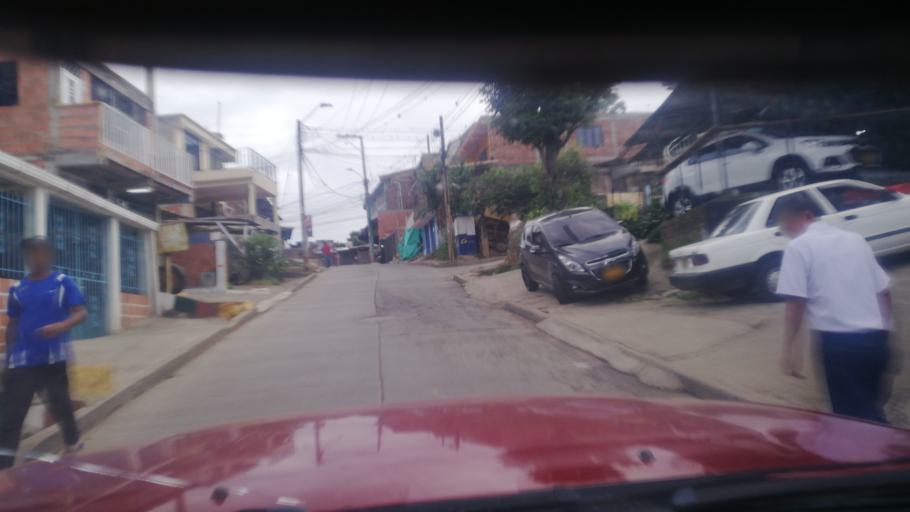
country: CO
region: Valle del Cauca
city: Cali
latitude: 3.4845
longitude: -76.5490
